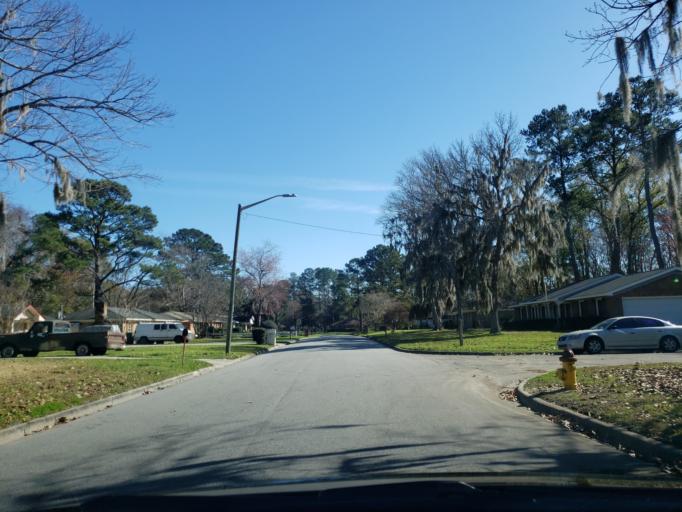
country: US
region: Georgia
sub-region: Chatham County
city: Montgomery
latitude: 31.9878
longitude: -81.1507
